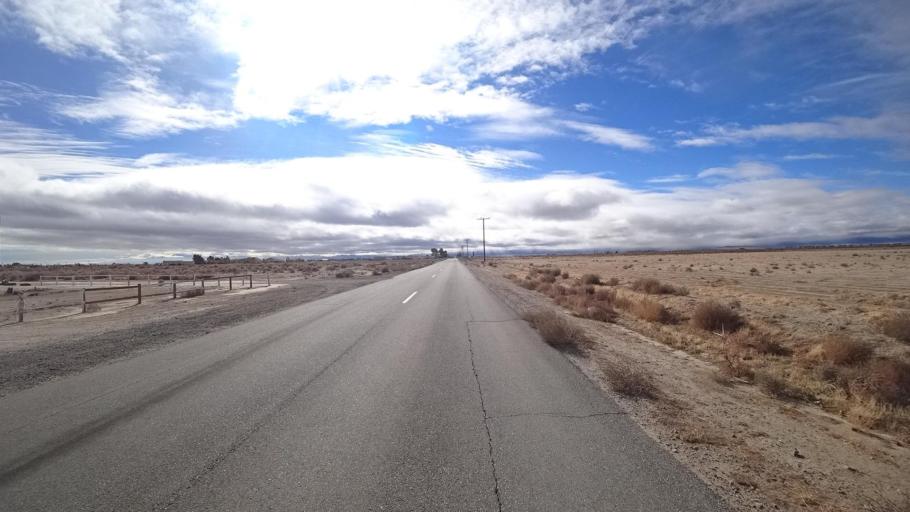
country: US
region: California
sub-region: Kern County
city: Rosamond
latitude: 34.8467
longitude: -118.2731
